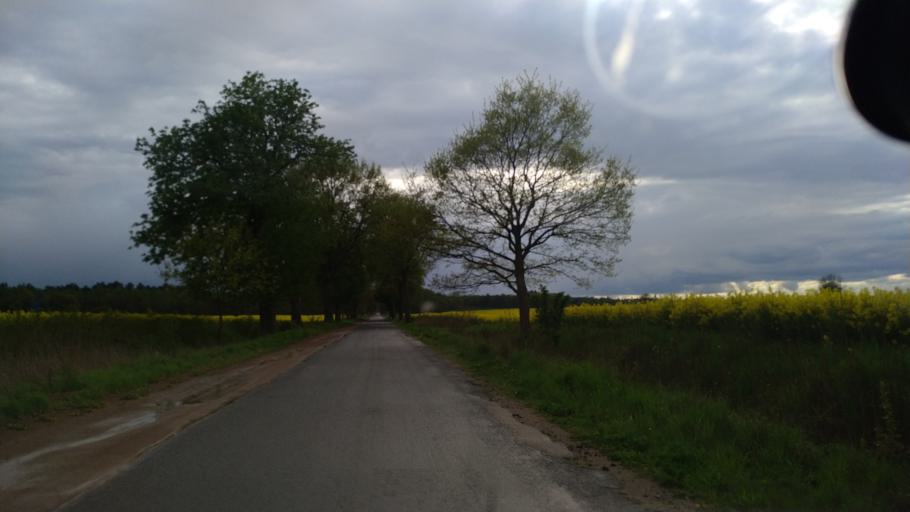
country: PL
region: Pomeranian Voivodeship
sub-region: Powiat starogardzki
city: Smetowo Graniczne
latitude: 53.7145
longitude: 18.6006
